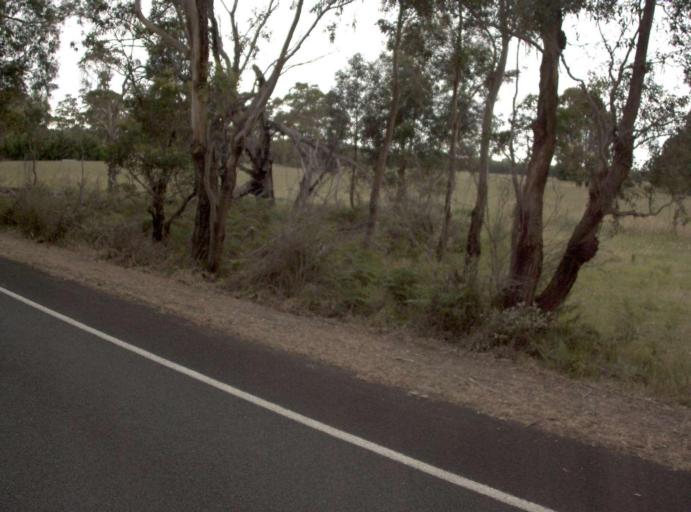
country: AU
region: Victoria
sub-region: Wellington
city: Sale
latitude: -38.4711
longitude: 146.9289
